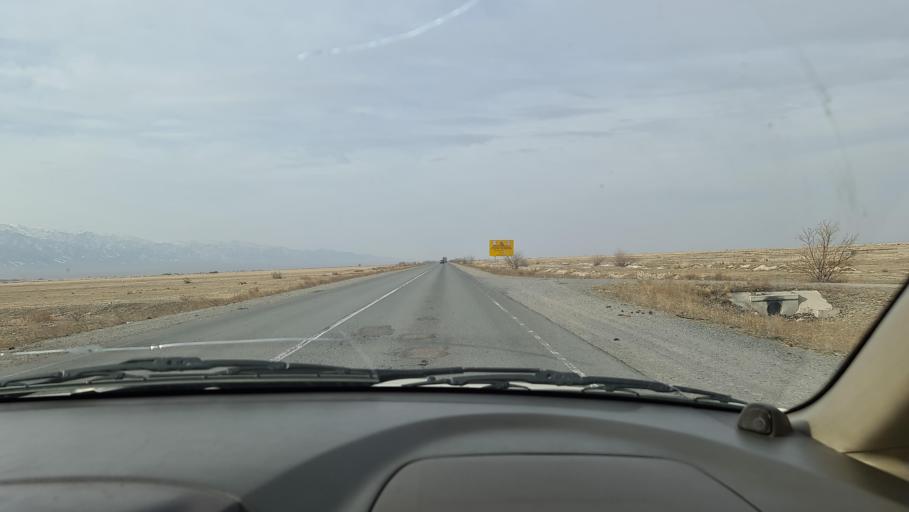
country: KG
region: Chuy
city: Tokmok
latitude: 43.3436
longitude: 75.5352
